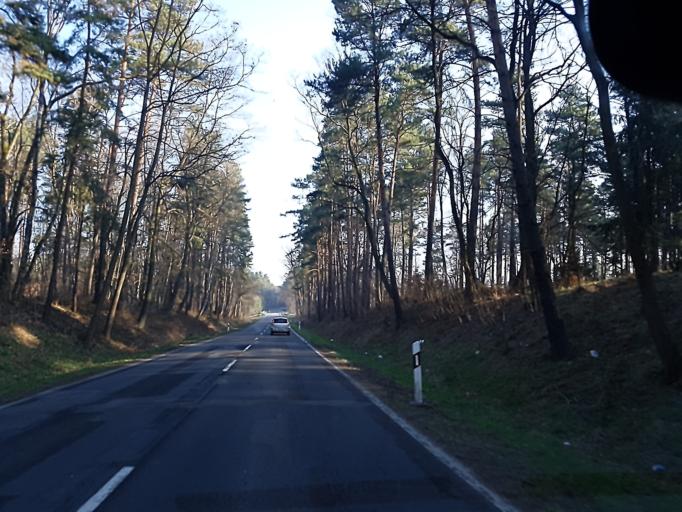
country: DE
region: Brandenburg
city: Bronkow
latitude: 51.7087
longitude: 13.9204
